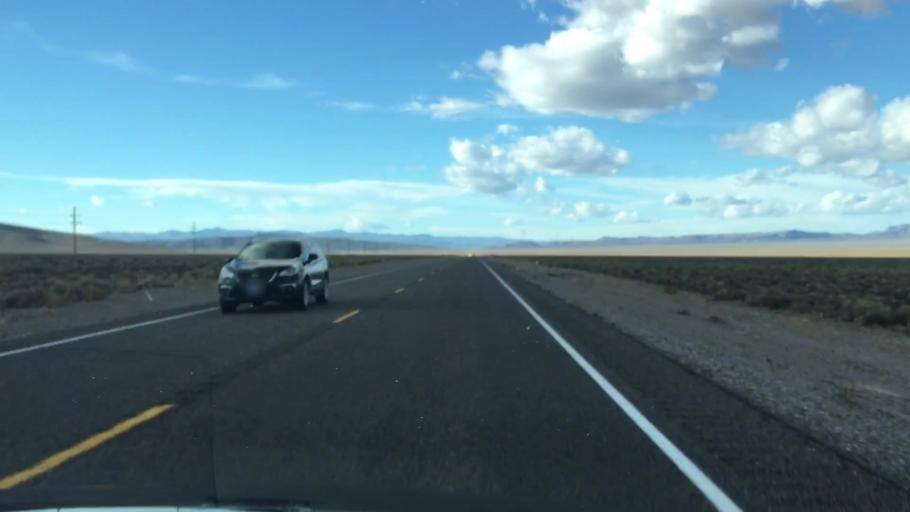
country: US
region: Nevada
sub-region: Nye County
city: Beatty
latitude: 37.1204
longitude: -116.8229
